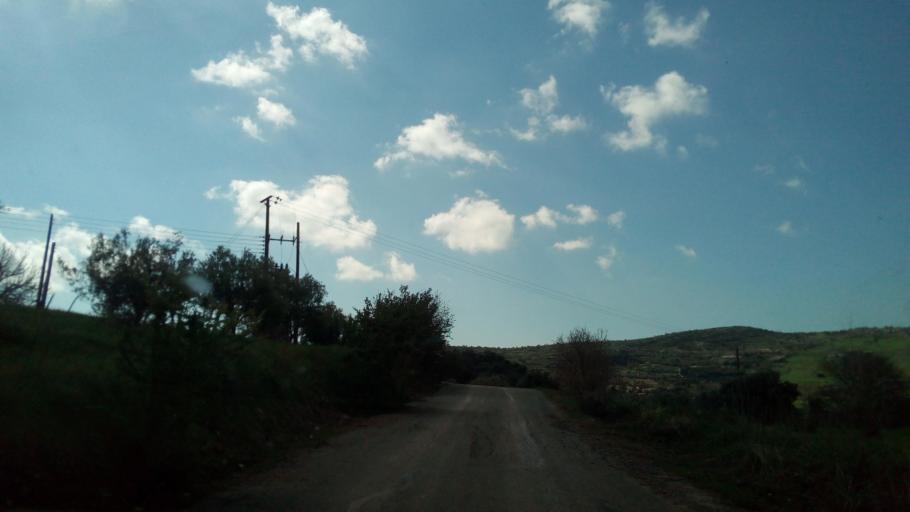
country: CY
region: Pafos
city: Mesogi
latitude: 34.7715
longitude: 32.5838
